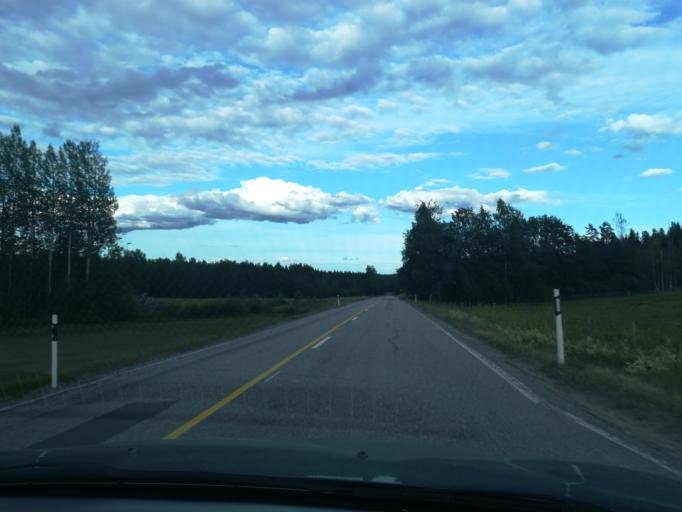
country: FI
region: Southern Savonia
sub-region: Mikkeli
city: Puumala
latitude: 61.5675
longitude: 28.0770
